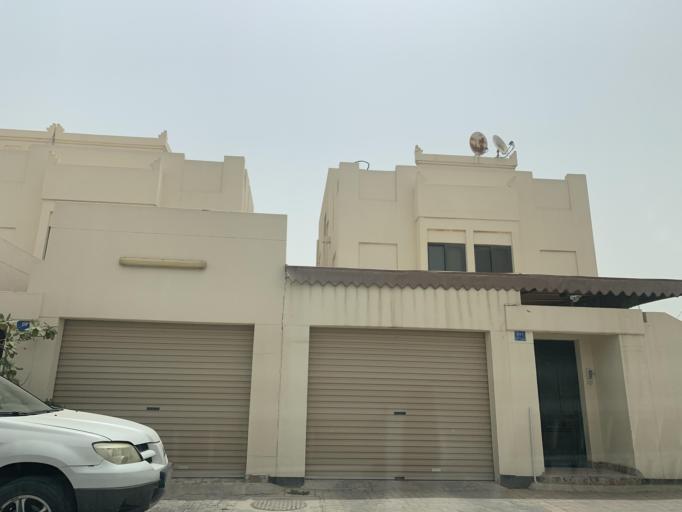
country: BH
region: Manama
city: Jidd Hafs
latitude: 26.2288
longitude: 50.5217
